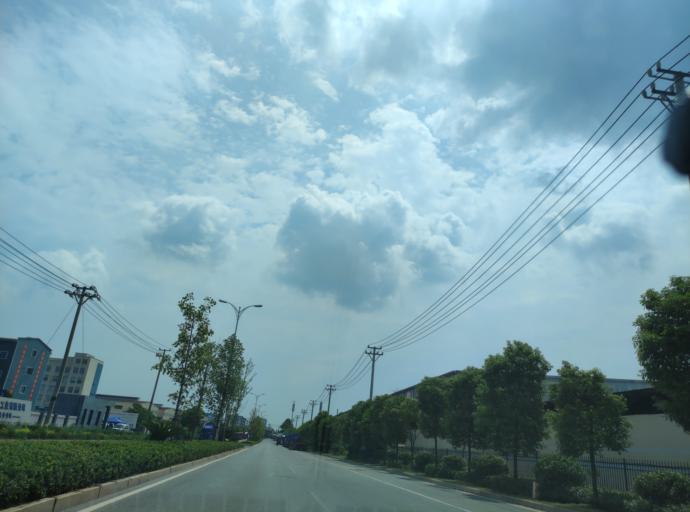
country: CN
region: Jiangxi Sheng
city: Yuannan
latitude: 27.6648
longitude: 114.0090
